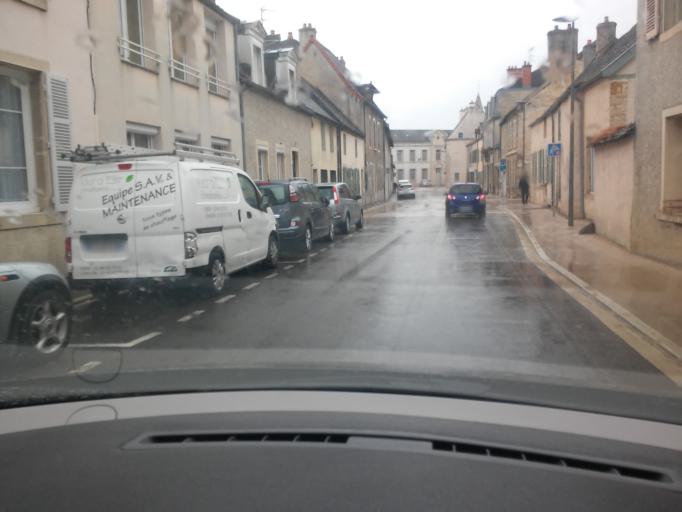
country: FR
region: Bourgogne
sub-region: Departement de la Cote-d'Or
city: Nuits-Saint-Georges
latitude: 47.1392
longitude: 4.9496
